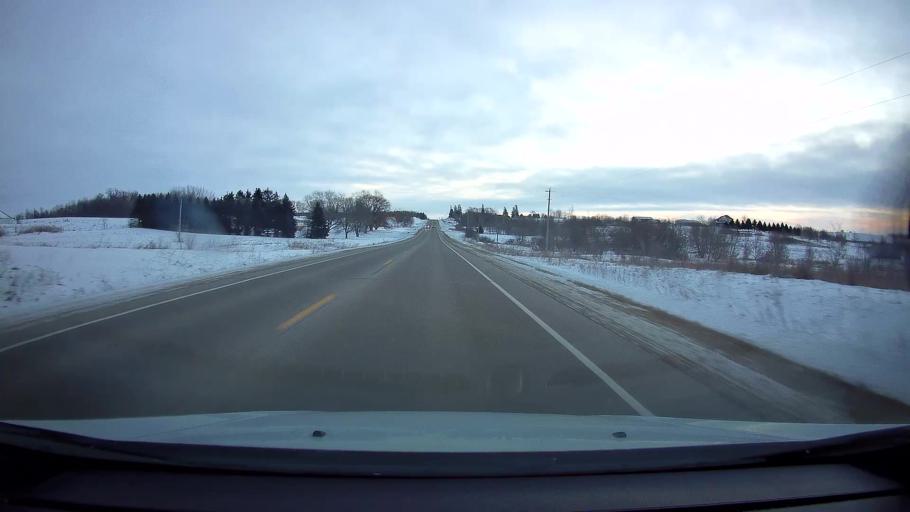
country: US
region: Wisconsin
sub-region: Saint Croix County
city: New Richmond
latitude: 45.1371
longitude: -92.5060
